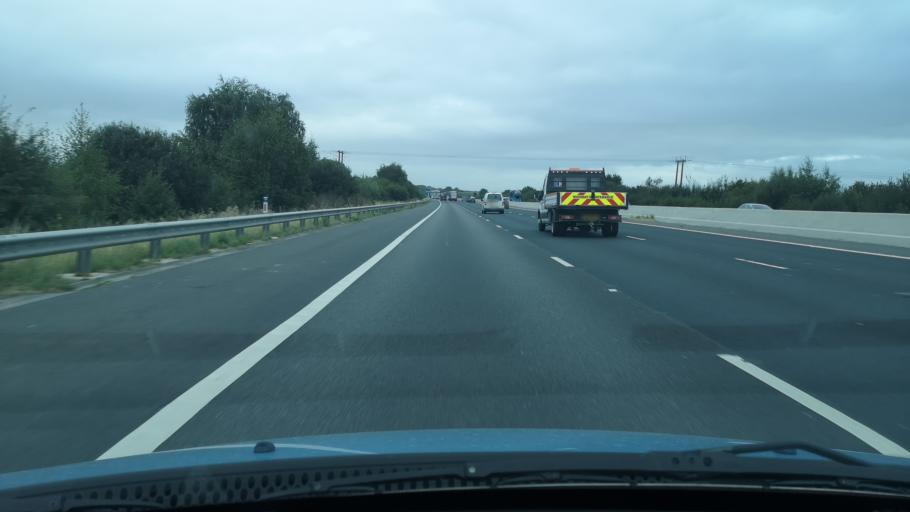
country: GB
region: England
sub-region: City and Borough of Wakefield
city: Knottingley
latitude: 53.6947
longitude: -1.2059
